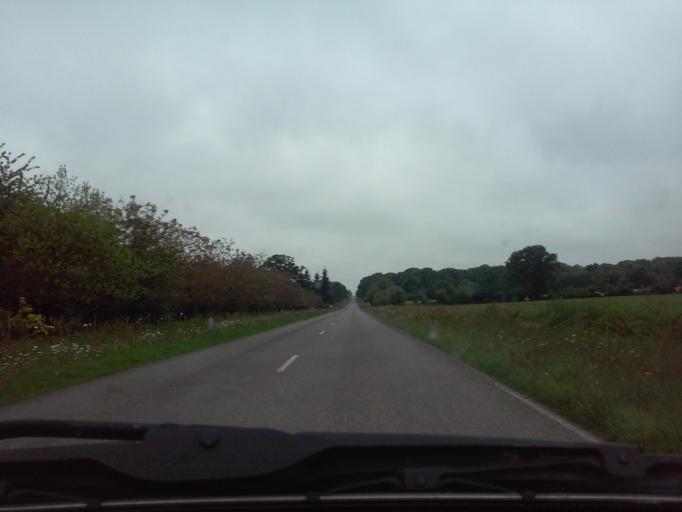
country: FR
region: Brittany
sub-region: Departement d'Ille-et-Vilaine
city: Le Pertre
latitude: 47.9620
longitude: -1.0026
